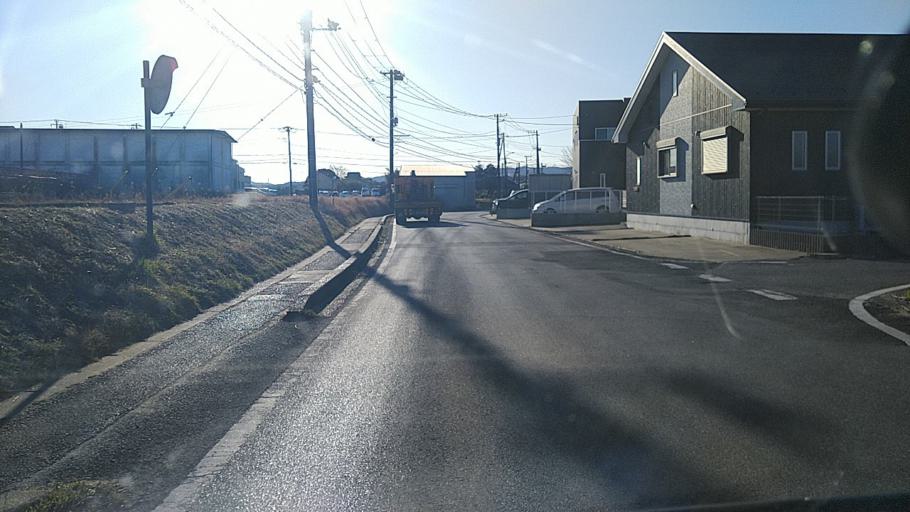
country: JP
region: Chiba
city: Kimitsu
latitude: 35.3196
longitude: 139.9033
